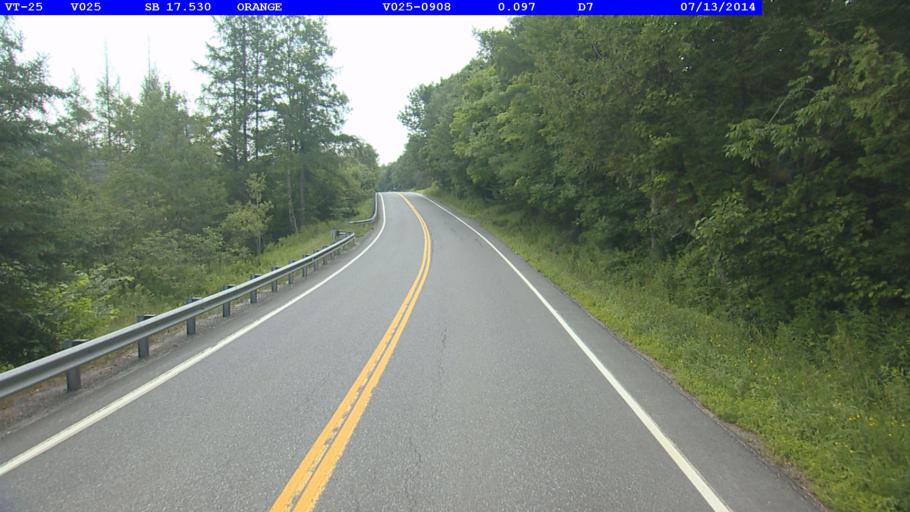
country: US
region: Vermont
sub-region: Washington County
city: South Barre
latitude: 44.1377
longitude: -72.3194
